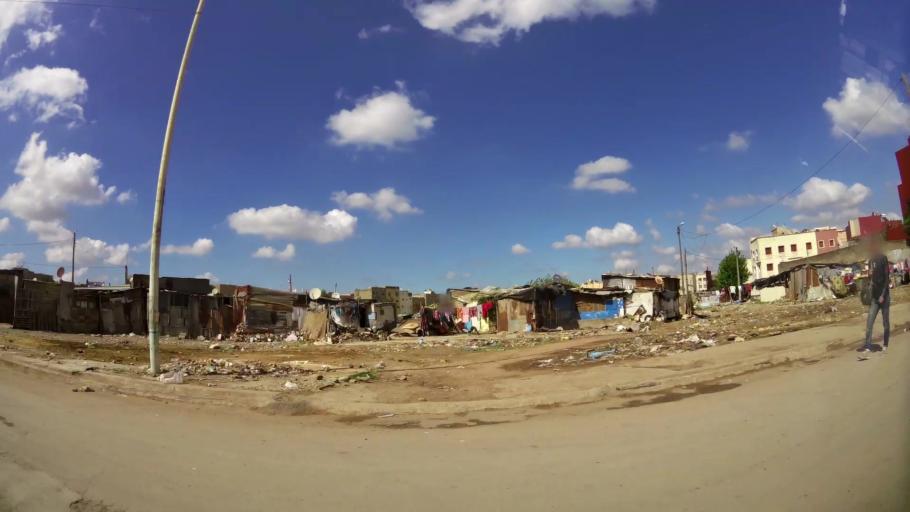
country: MA
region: Grand Casablanca
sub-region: Mediouna
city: Mediouna
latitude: 33.4524
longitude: -7.5142
